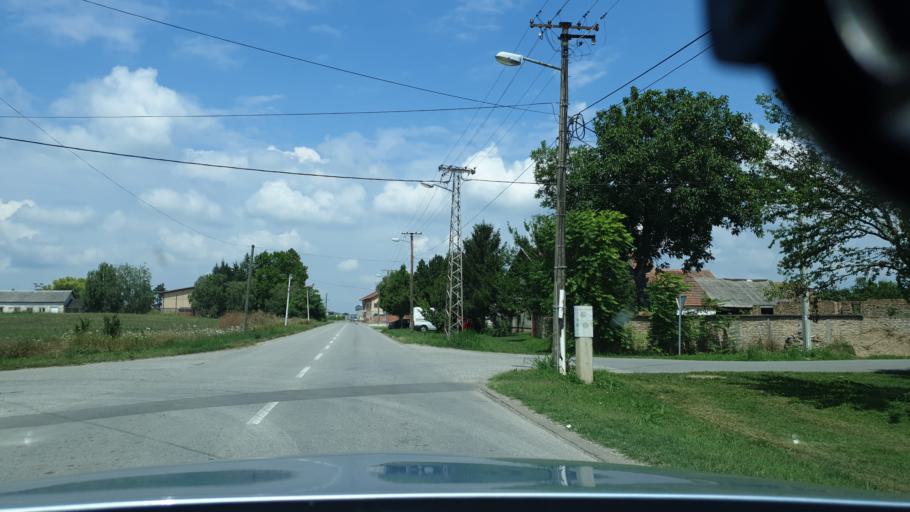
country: RS
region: Autonomna Pokrajina Vojvodina
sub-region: Juznobacki Okrug
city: Kovilj
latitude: 45.2401
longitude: 20.0261
